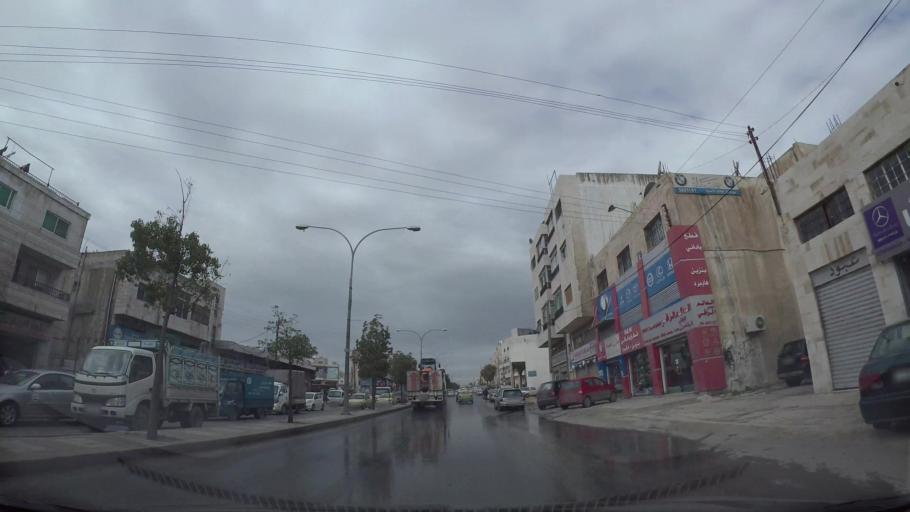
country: JO
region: Amman
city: Wadi as Sir
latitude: 31.9462
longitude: 35.8377
